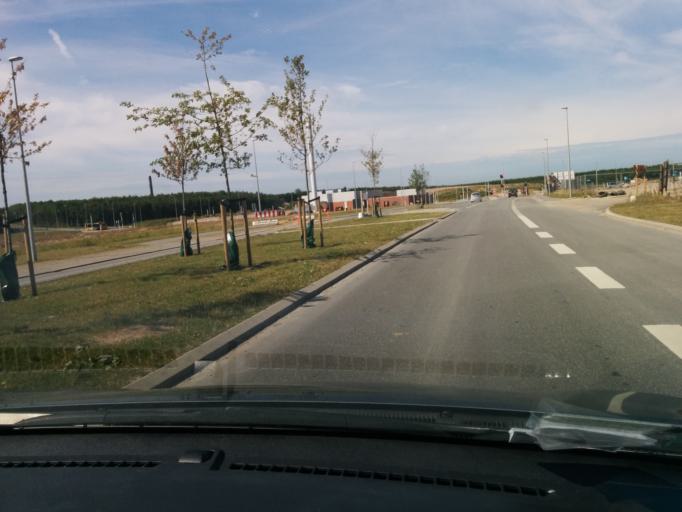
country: DK
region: Central Jutland
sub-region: Arhus Kommune
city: Arhus
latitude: 56.1876
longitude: 10.1728
